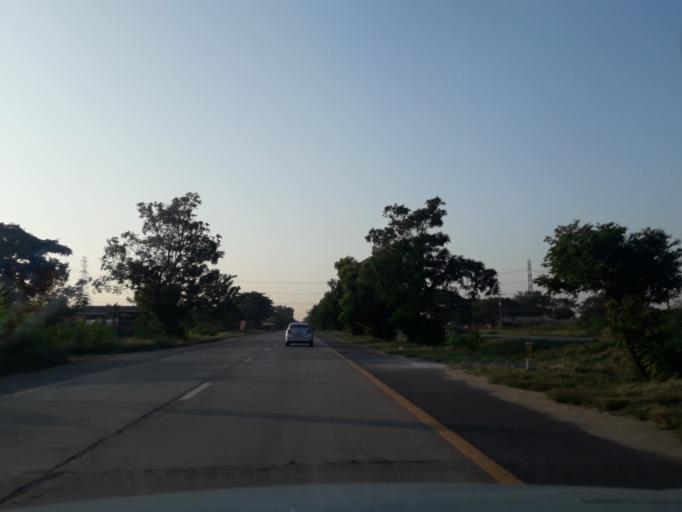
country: TH
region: Phra Nakhon Si Ayutthaya
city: Bang Pa-in
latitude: 14.2760
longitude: 100.5294
